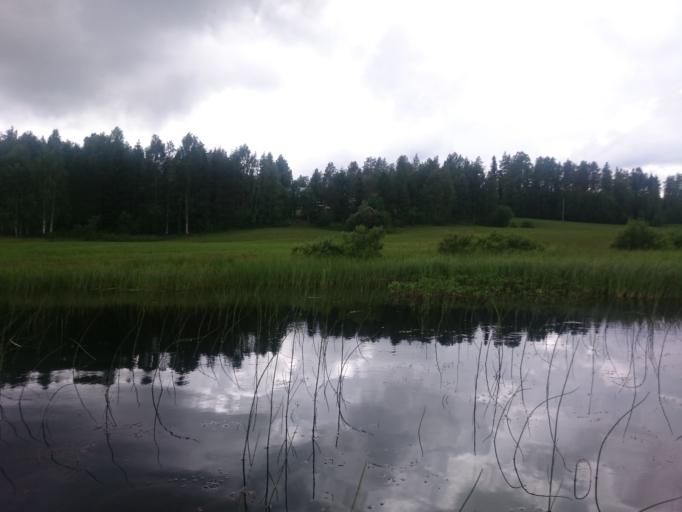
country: SE
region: Vaesternorrland
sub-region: OErnskoeldsviks Kommun
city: Ornskoldsvik
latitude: 63.6513
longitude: 18.6086
